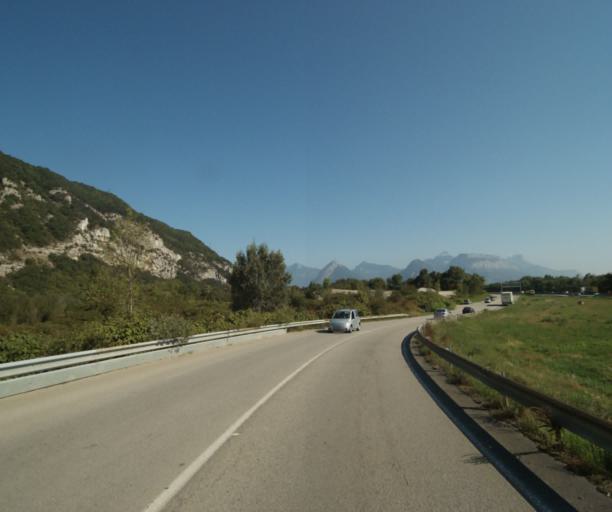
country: FR
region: Rhone-Alpes
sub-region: Departement de l'Isere
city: Claix
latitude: 45.1366
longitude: 5.6891
